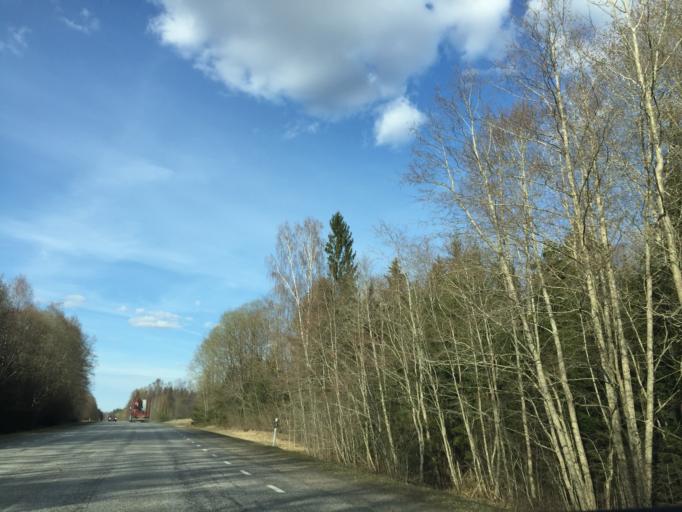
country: EE
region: Tartu
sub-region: Elva linn
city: Elva
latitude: 58.1148
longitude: 26.5112
